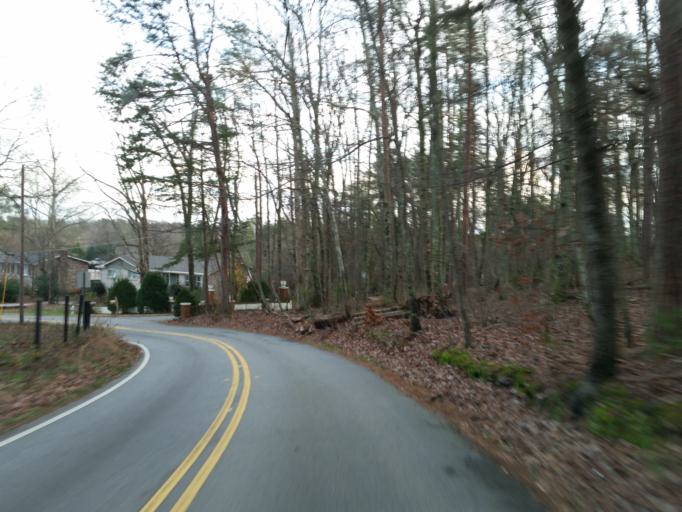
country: US
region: Georgia
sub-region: Cobb County
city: Marietta
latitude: 33.9801
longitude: -84.4911
